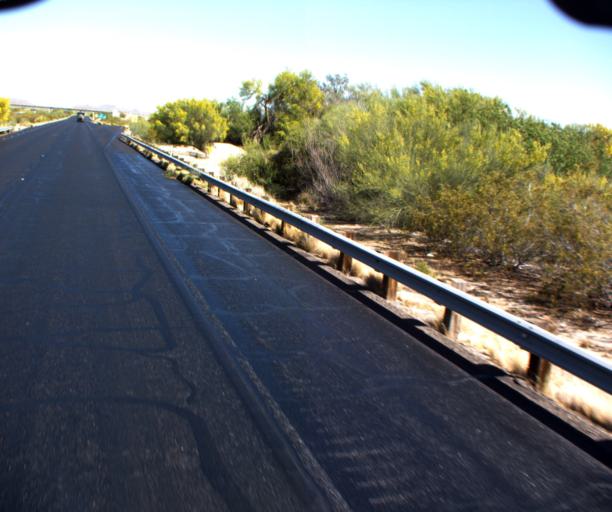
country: US
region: Arizona
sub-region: Pinal County
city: Maricopa
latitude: 32.8424
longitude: -112.2595
